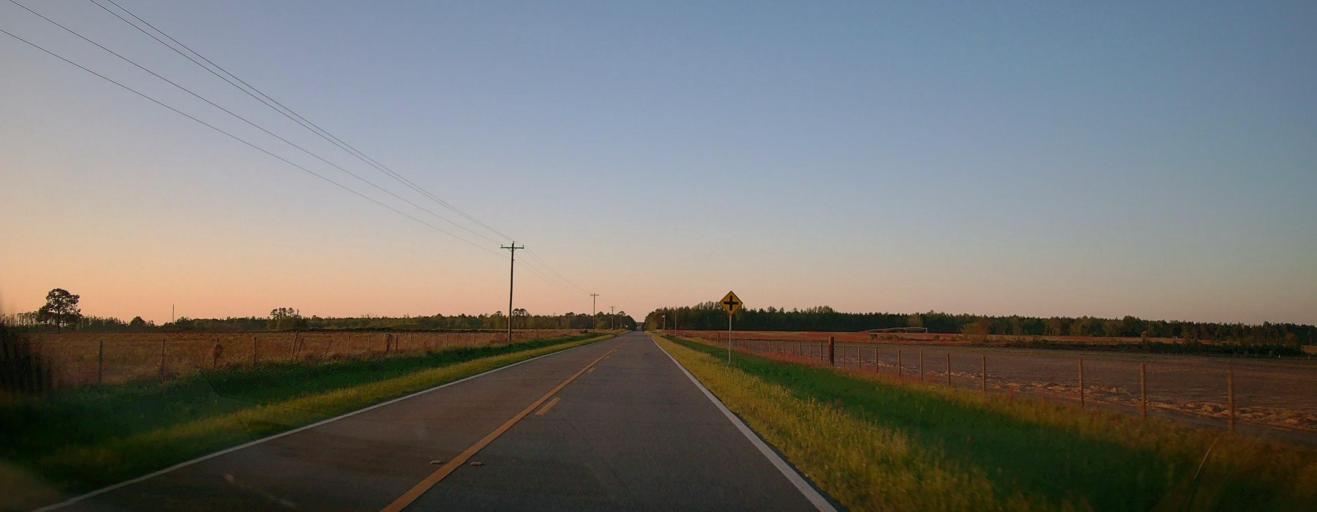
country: US
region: Georgia
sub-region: Ben Hill County
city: Fitzgerald
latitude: 31.7292
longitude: -83.3098
